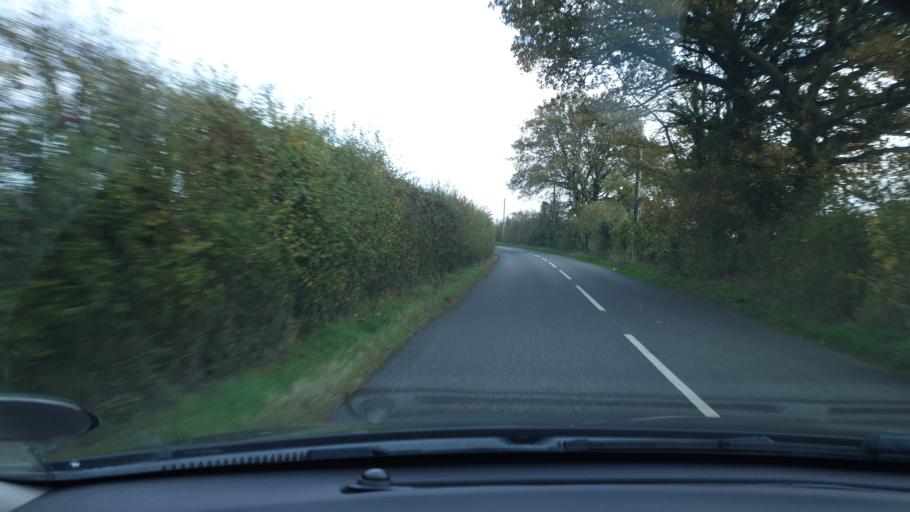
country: GB
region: England
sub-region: Essex
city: Mistley
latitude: 51.9270
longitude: 1.1182
